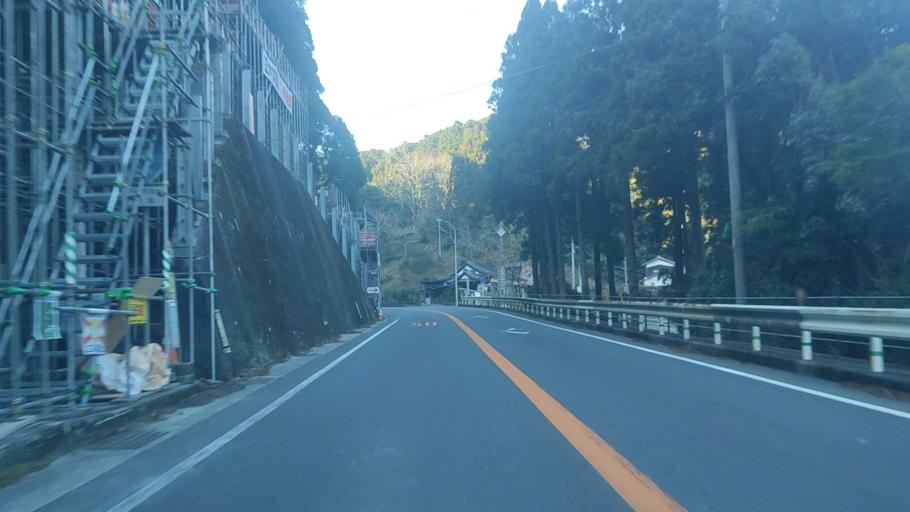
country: JP
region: Oita
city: Tsukumiura
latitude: 32.9995
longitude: 131.8139
